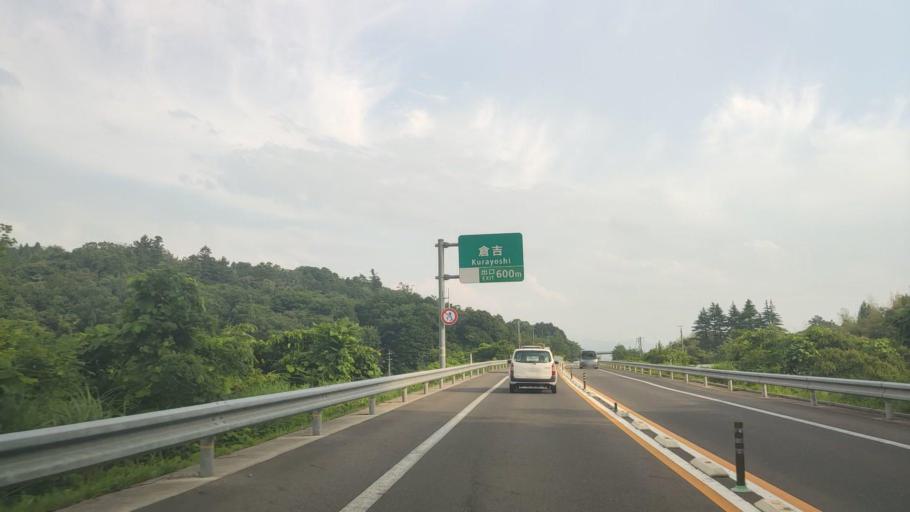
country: JP
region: Tottori
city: Kurayoshi
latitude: 35.4561
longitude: 133.8107
